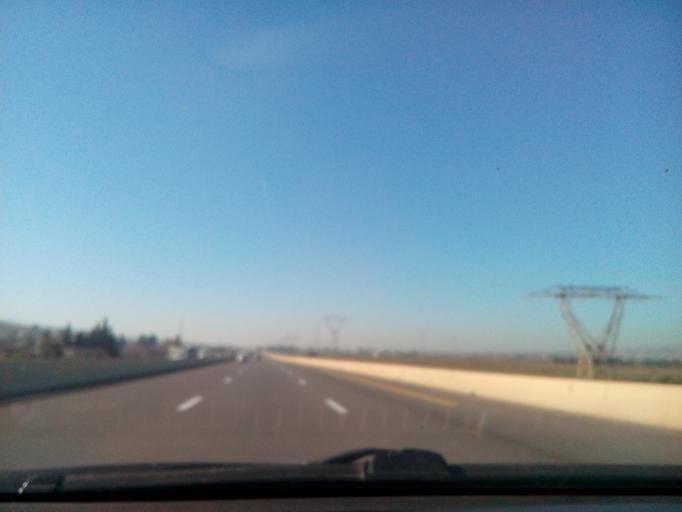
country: DZ
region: Chlef
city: Boukadir
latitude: 36.0484
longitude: 1.1085
